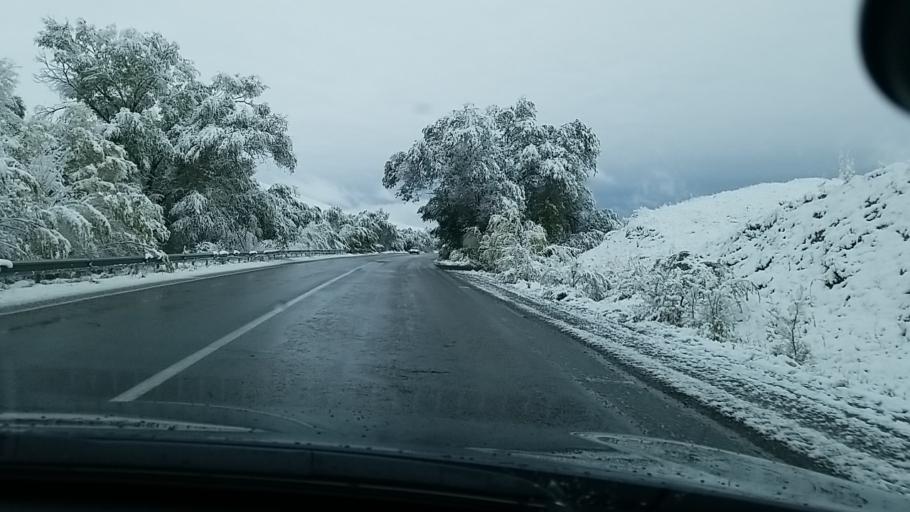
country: KZ
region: Almaty Oblysy
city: Burunday
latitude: 43.2899
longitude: 76.2487
